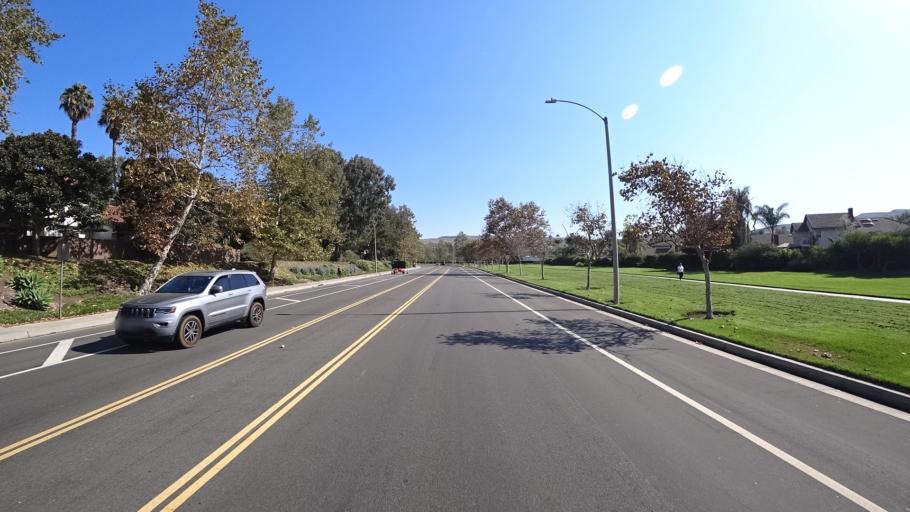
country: US
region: California
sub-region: Orange County
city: San Juan Capistrano
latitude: 33.4702
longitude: -117.6315
